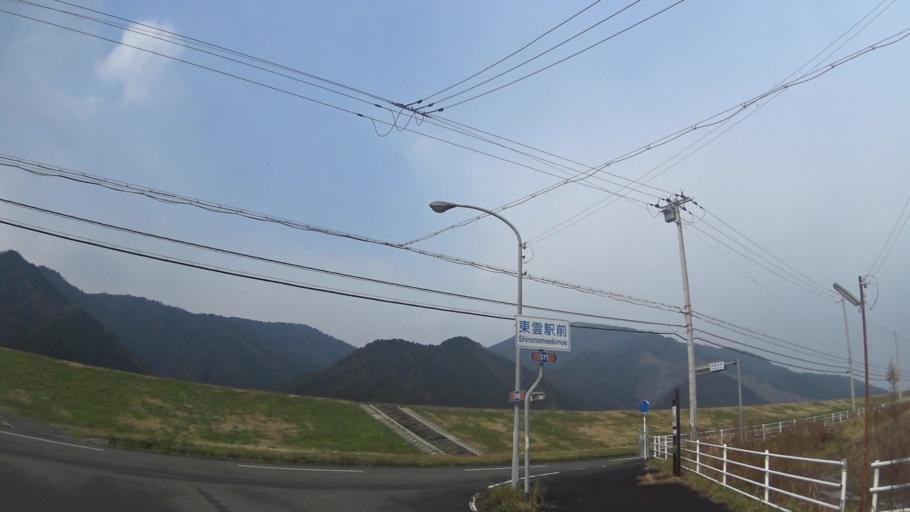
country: JP
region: Kyoto
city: Maizuru
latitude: 35.4753
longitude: 135.2823
